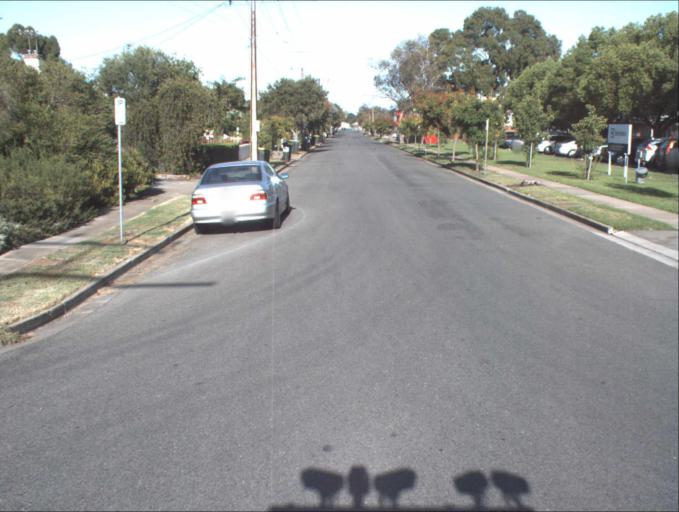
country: AU
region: South Australia
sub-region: Prospect
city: Prospect
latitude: -34.8852
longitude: 138.5803
